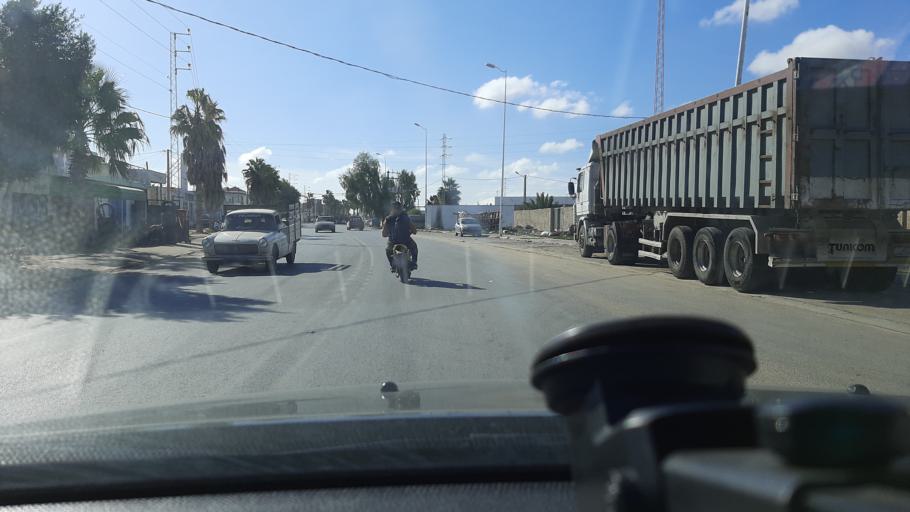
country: TN
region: Safaqis
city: Sfax
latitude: 34.8102
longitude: 10.7075
